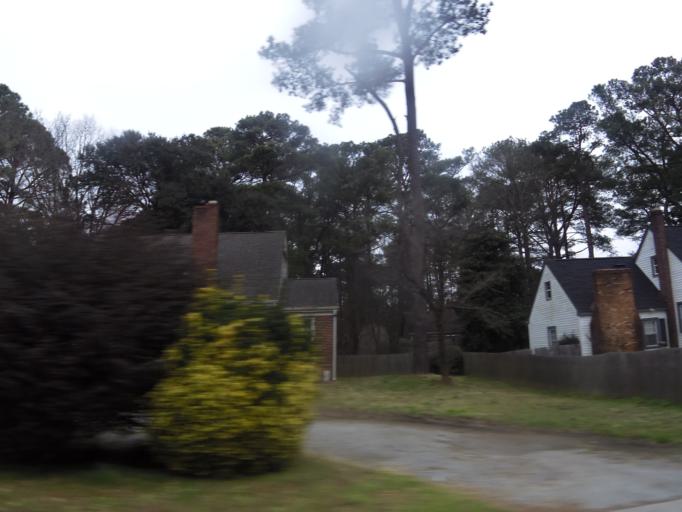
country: US
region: Virginia
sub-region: City of Portsmouth
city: Portsmouth Heights
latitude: 36.8460
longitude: -76.3701
